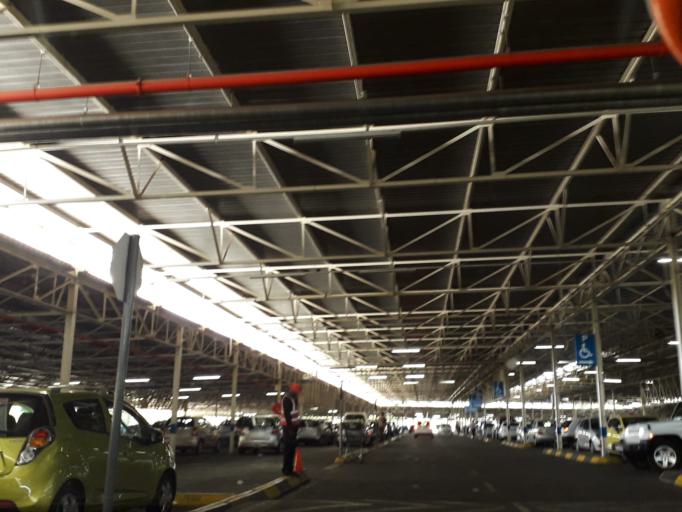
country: ZA
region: Gauteng
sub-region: City of Johannesburg Metropolitan Municipality
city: Johannesburg
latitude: -26.1469
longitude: 28.0794
